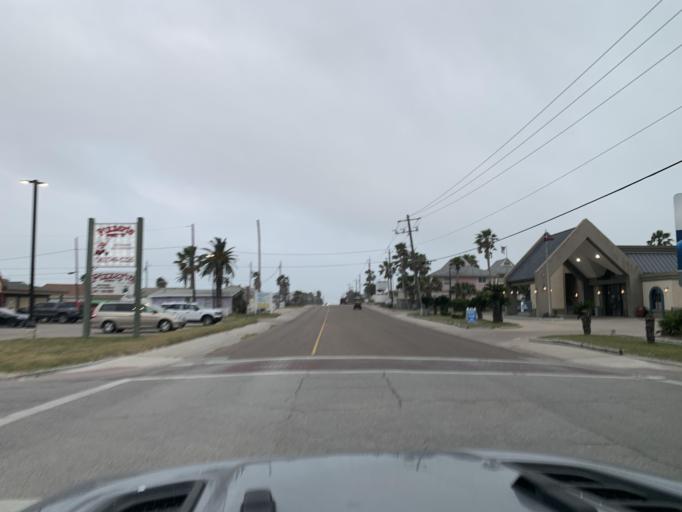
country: US
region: Texas
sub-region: Nueces County
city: Port Aransas
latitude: 27.8265
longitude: -97.0647
